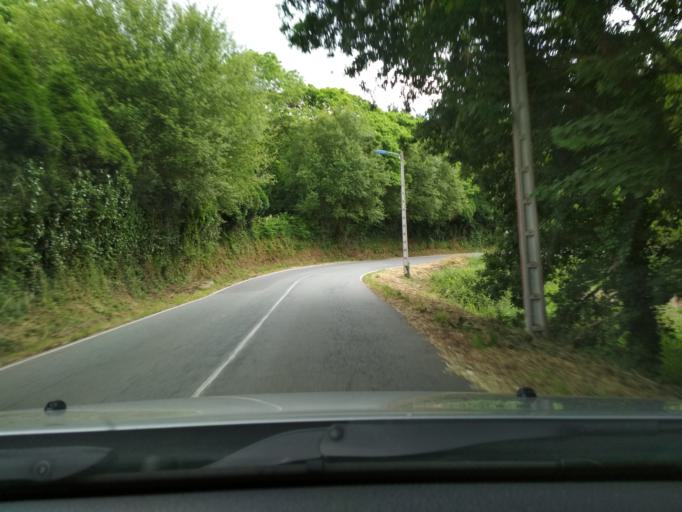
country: ES
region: Galicia
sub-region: Provincia da Coruna
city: Culleredo
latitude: 43.2497
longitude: -8.4103
